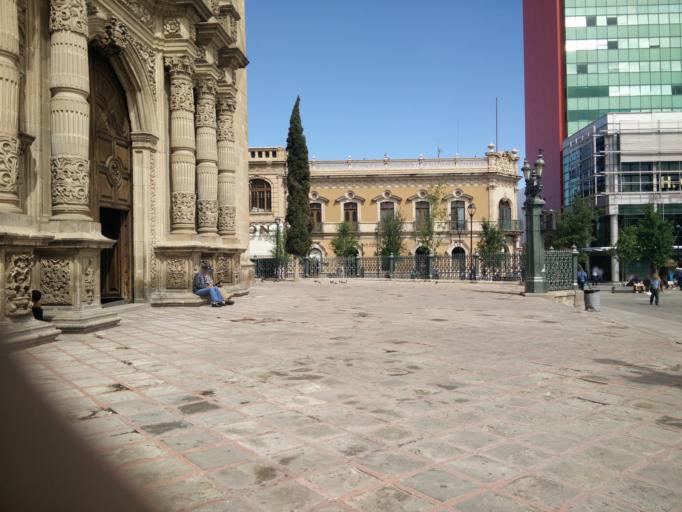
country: MX
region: Chihuahua
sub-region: Chihuahua
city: Chihuahua
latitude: 28.6360
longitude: -106.0770
